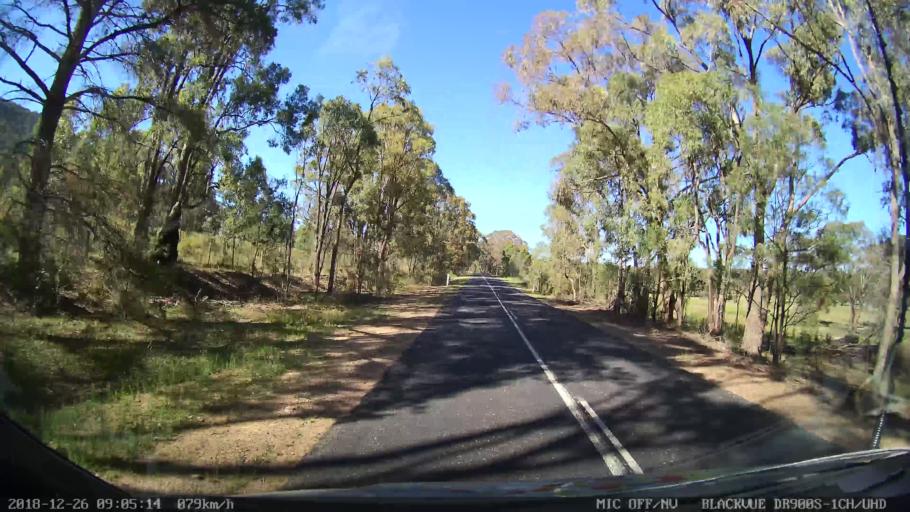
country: AU
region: New South Wales
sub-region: Mid-Western Regional
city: Kandos
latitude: -32.6808
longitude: 150.0096
